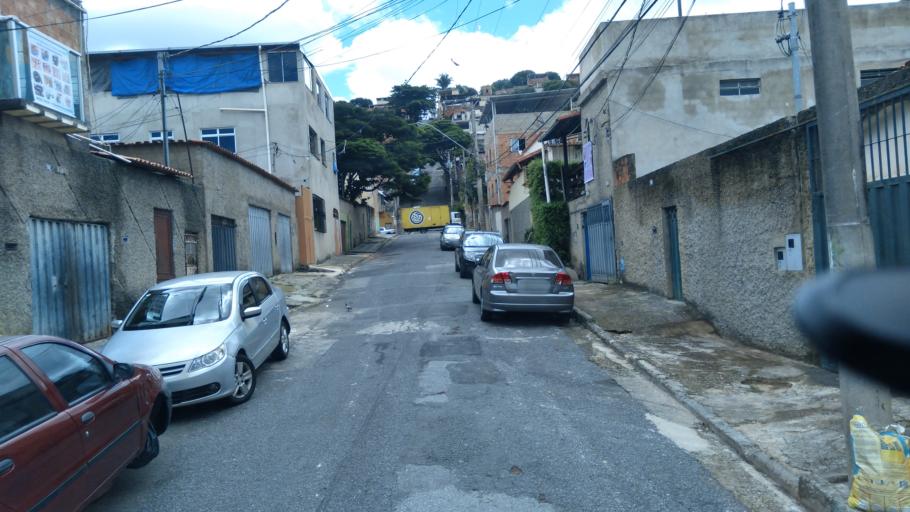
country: BR
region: Minas Gerais
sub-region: Belo Horizonte
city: Belo Horizonte
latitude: -19.8980
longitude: -43.8867
